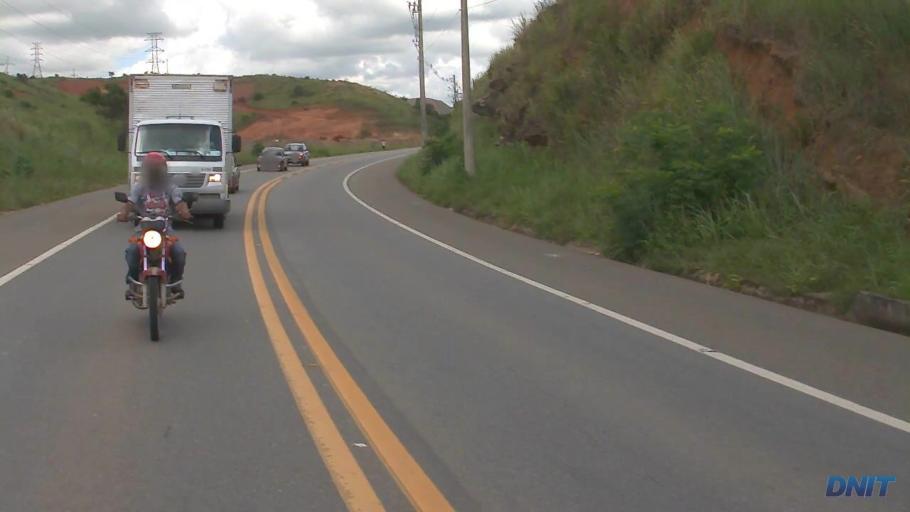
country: BR
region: Minas Gerais
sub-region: Governador Valadares
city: Governador Valadares
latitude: -18.8727
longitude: -41.9922
